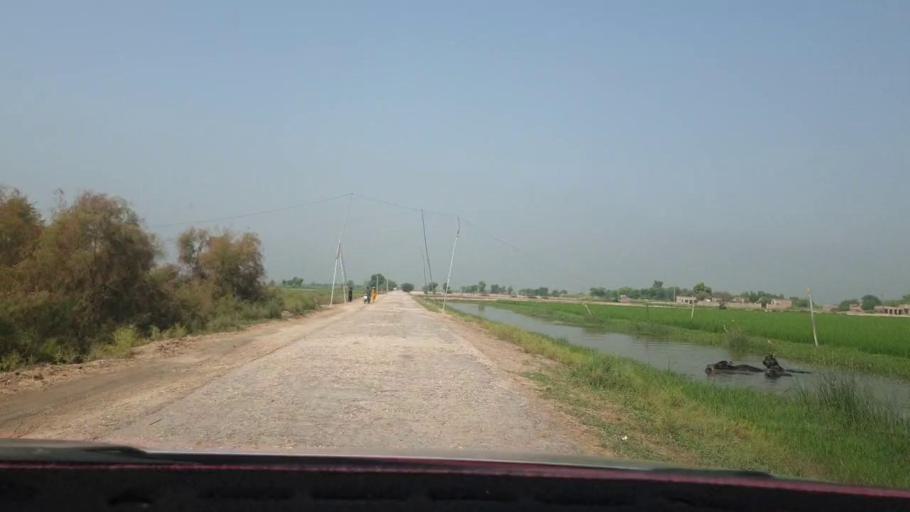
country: PK
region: Sindh
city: Nasirabad
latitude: 27.4326
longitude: 67.8920
